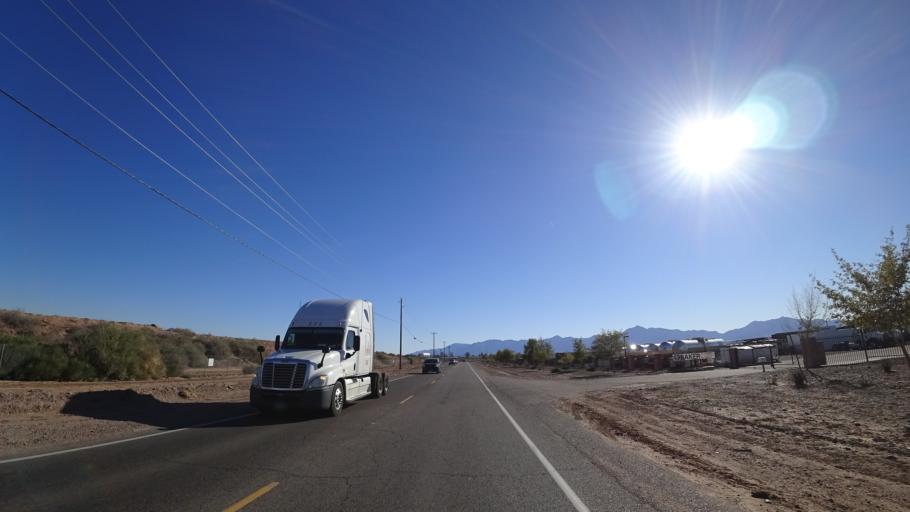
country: US
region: Arizona
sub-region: Maricopa County
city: Laveen
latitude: 33.4037
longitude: -112.2042
